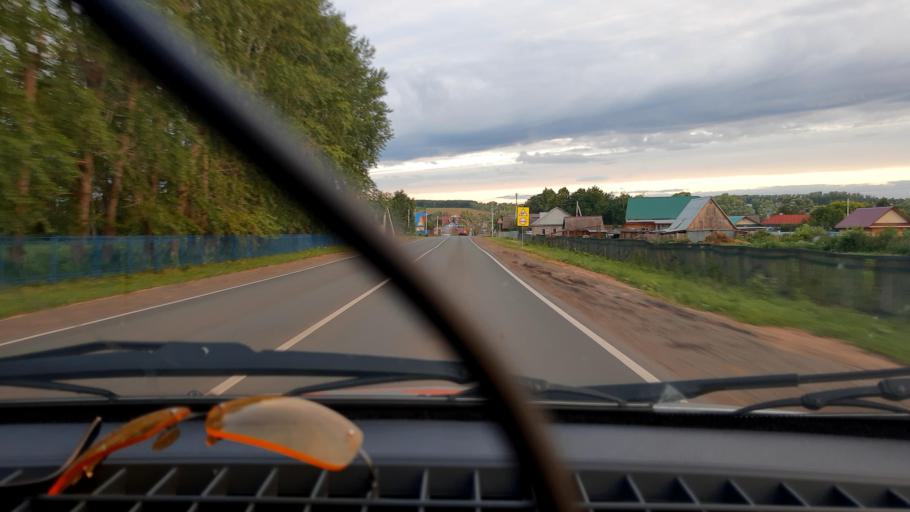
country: RU
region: Bashkortostan
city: Avdon
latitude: 54.5643
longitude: 55.5954
